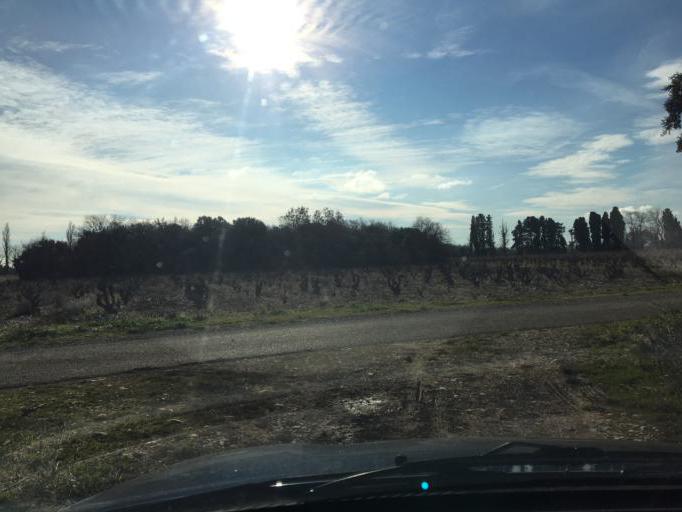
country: FR
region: Provence-Alpes-Cote d'Azur
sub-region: Departement du Vaucluse
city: Camaret-sur-Aigues
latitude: 44.1479
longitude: 4.8954
